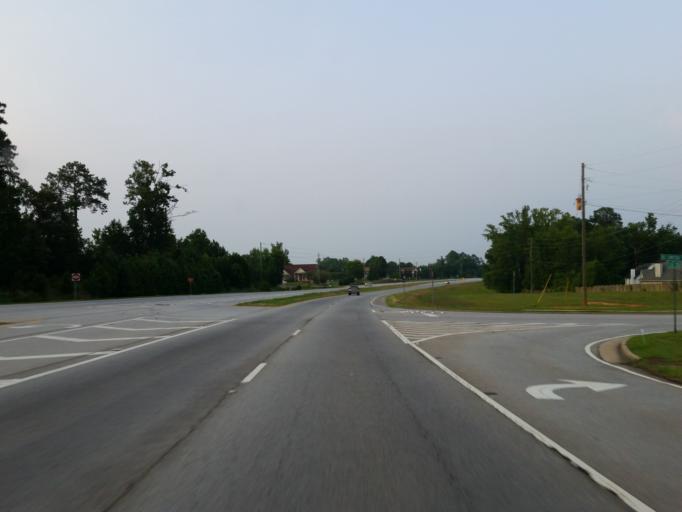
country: US
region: Georgia
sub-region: Henry County
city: McDonough
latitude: 33.4093
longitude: -84.2104
